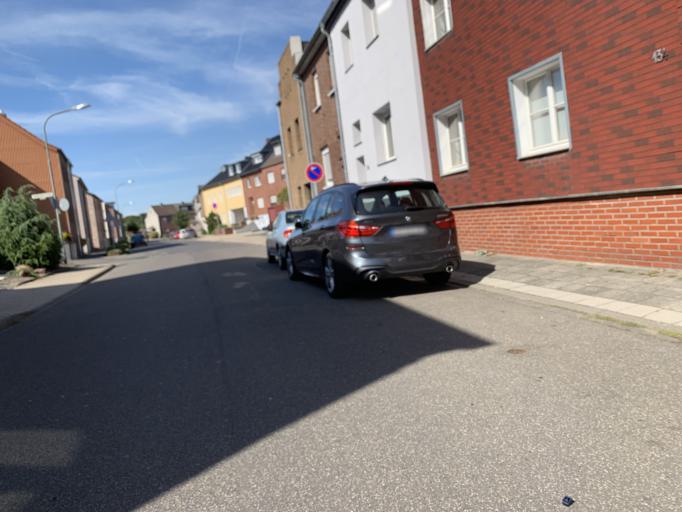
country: DE
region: North Rhine-Westphalia
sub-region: Regierungsbezirk Koln
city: Dueren
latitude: 50.8008
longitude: 6.4315
